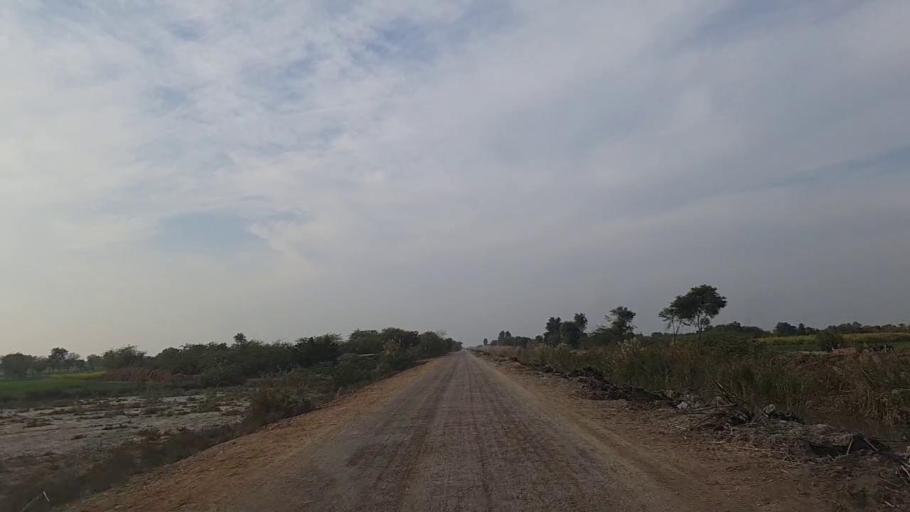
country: PK
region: Sindh
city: Daur
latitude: 26.4925
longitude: 68.4562
